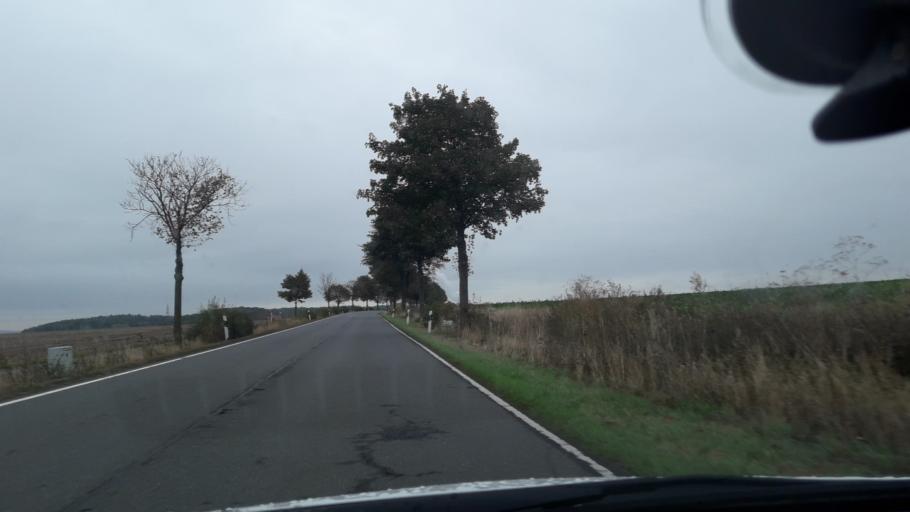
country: DE
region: Lower Saxony
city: Liebenburg
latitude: 52.0214
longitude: 10.4506
